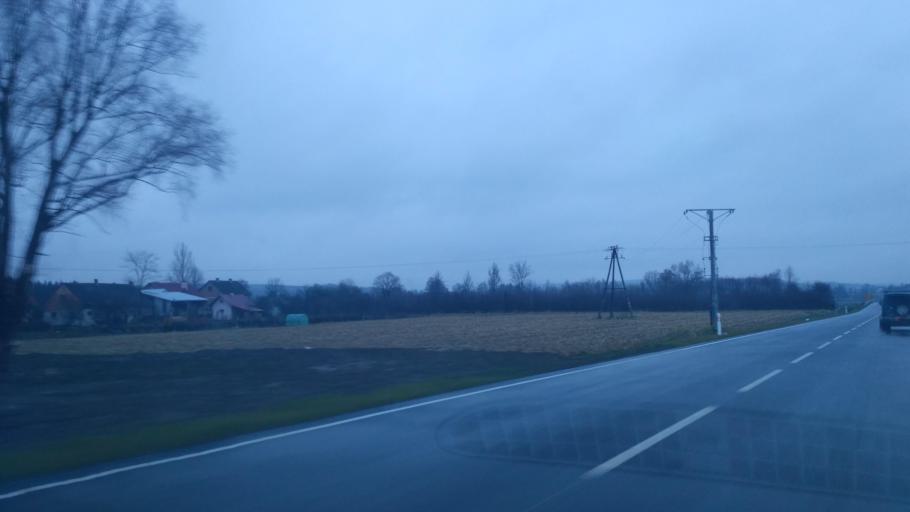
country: PL
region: Subcarpathian Voivodeship
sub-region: Powiat rzeszowski
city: Dynow
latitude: 49.8246
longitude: 22.2412
